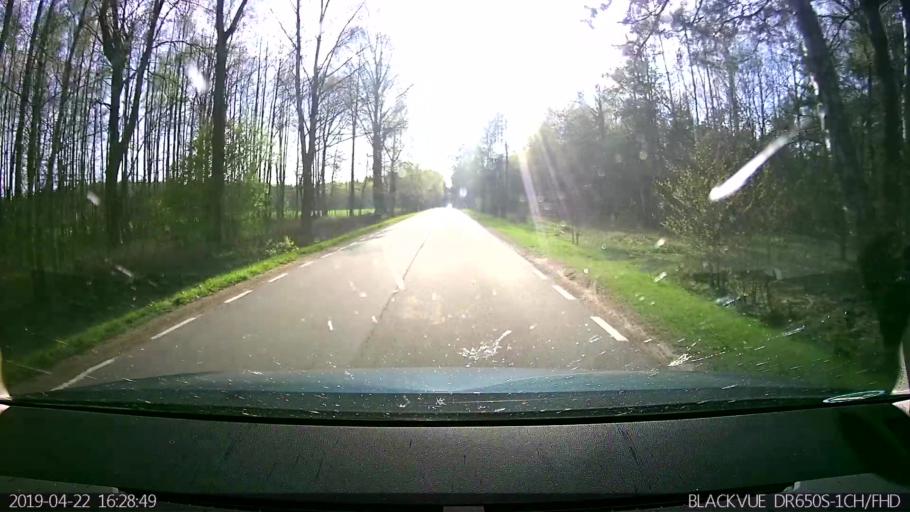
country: PL
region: Podlasie
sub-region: Powiat siemiatycki
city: Milejczyce
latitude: 52.5385
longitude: 23.1754
